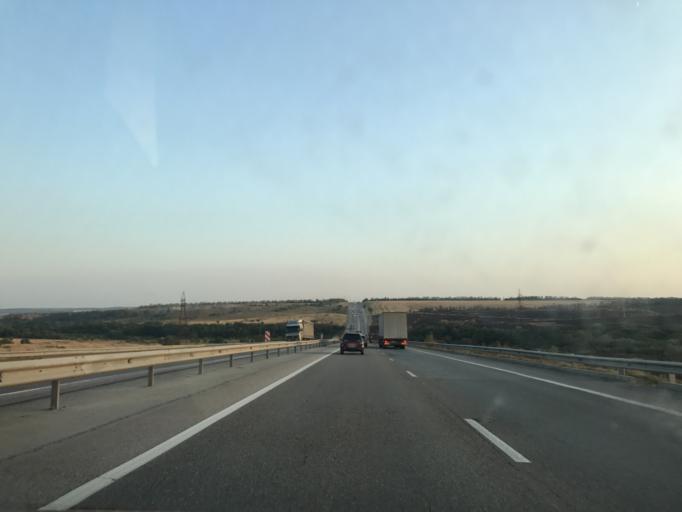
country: RU
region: Rostov
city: Gornyy
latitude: 47.9277
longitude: 40.2184
